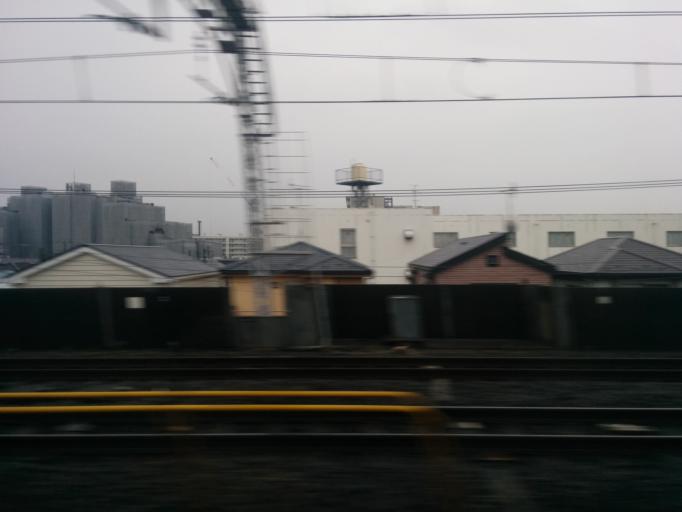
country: JP
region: Chiba
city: Funabashi
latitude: 35.7156
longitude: 139.9404
